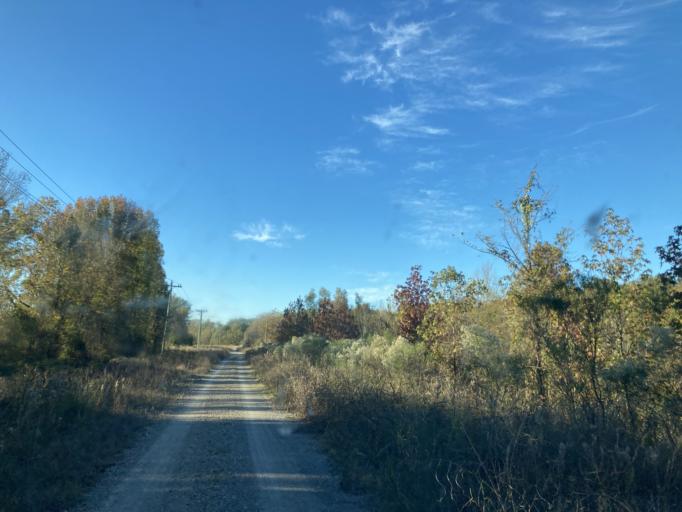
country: US
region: Mississippi
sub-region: Yazoo County
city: Yazoo City
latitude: 32.8934
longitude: -90.4329
